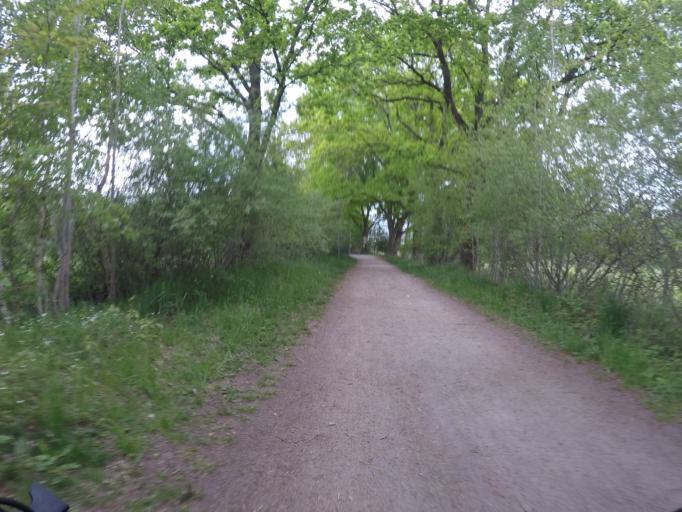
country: DE
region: Schleswig-Holstein
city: Henstedt-Ulzburg
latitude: 53.7584
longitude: 10.0158
